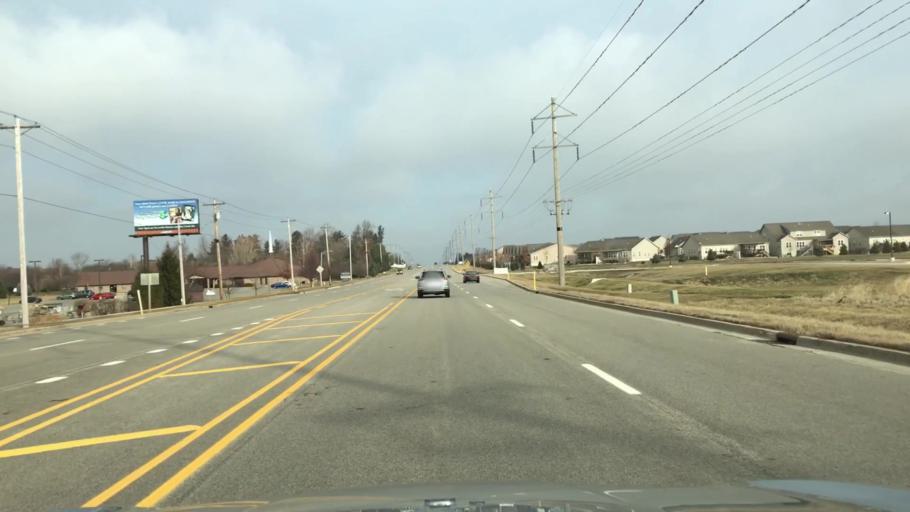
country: US
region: Illinois
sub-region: McLean County
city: Normal
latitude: 40.5037
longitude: -88.9027
